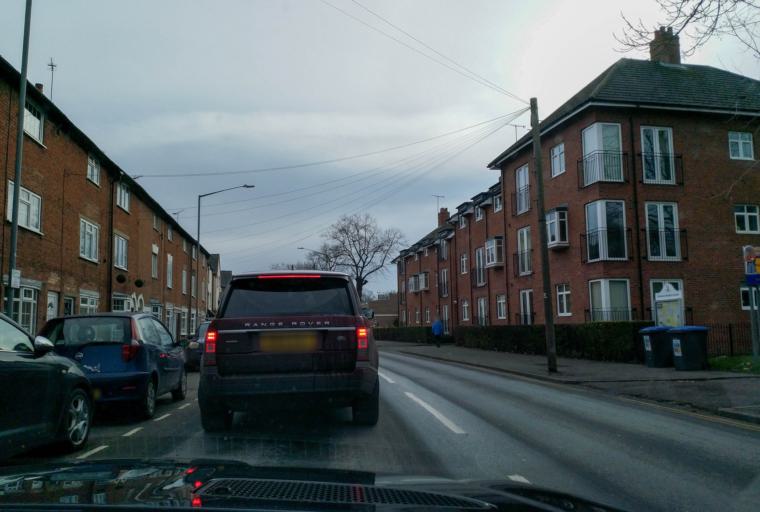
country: GB
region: England
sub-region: Warwickshire
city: Warwick
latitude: 52.2852
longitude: -1.5805
